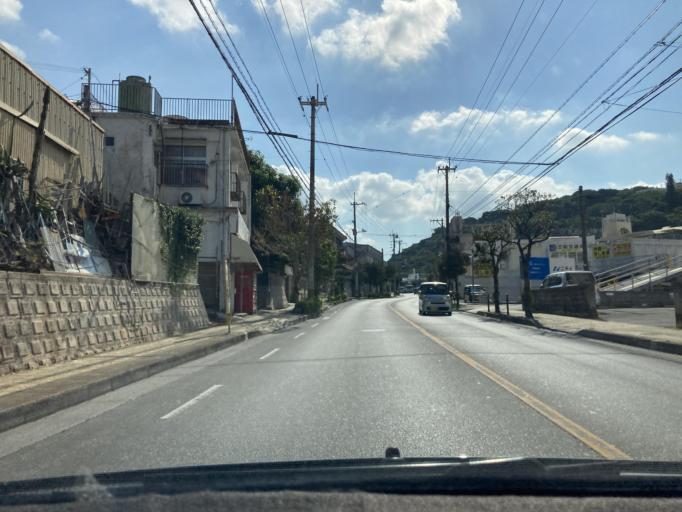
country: JP
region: Okinawa
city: Naha-shi
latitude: 26.2153
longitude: 127.7127
